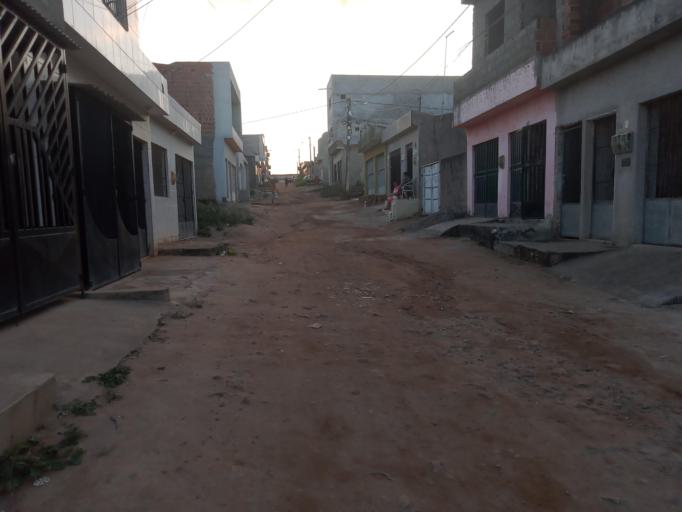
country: BR
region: Pernambuco
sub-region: Vitoria De Santo Antao
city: Vitoria de Santo Antao
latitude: -8.1248
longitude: -35.2786
